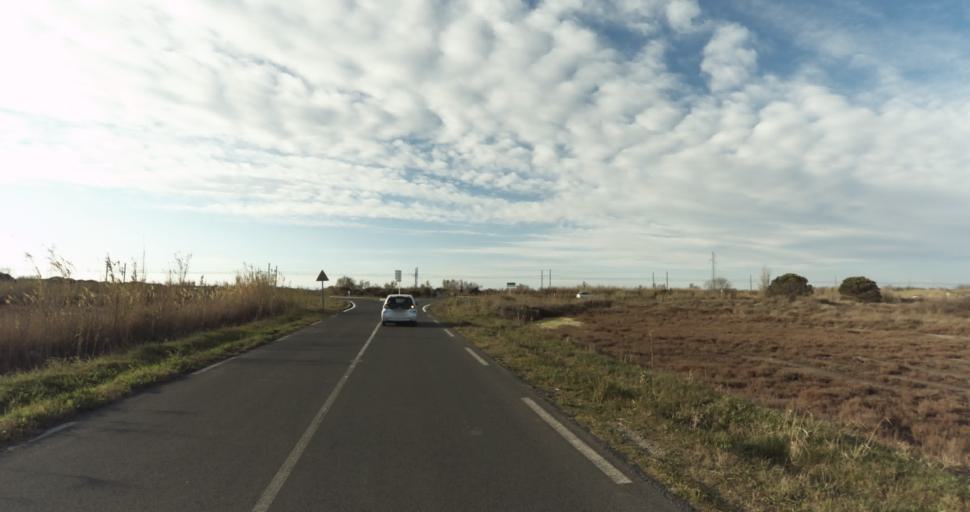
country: FR
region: Languedoc-Roussillon
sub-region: Departement de l'Herault
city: Marseillan
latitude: 43.3283
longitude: 3.5596
